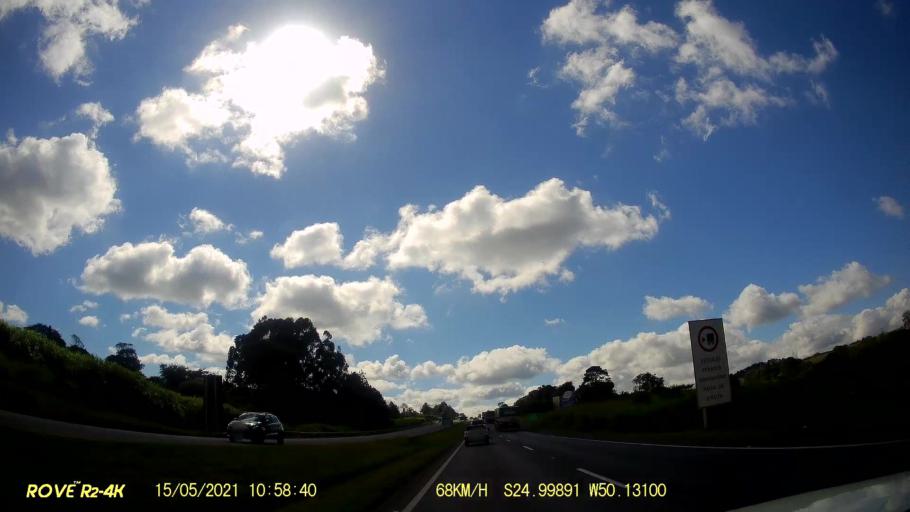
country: BR
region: Parana
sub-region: Carambei
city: Carambei
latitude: -24.9990
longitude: -50.1311
